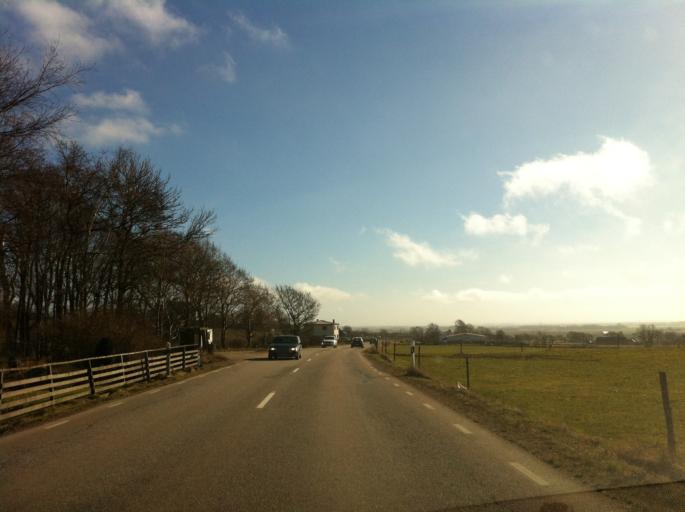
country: SE
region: Skane
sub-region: Bastads Kommun
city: Forslov
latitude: 56.3402
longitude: 12.8243
